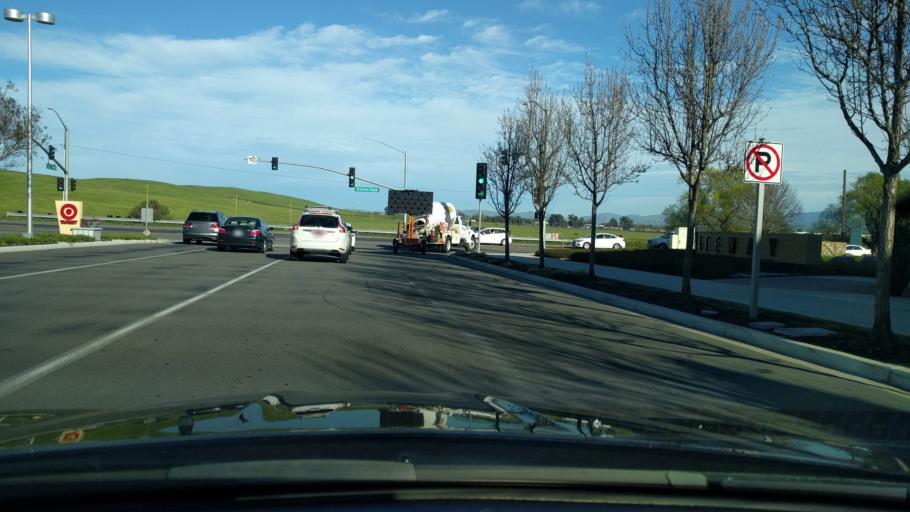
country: US
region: California
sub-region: Alameda County
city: Pleasanton
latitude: 37.7047
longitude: -121.8515
